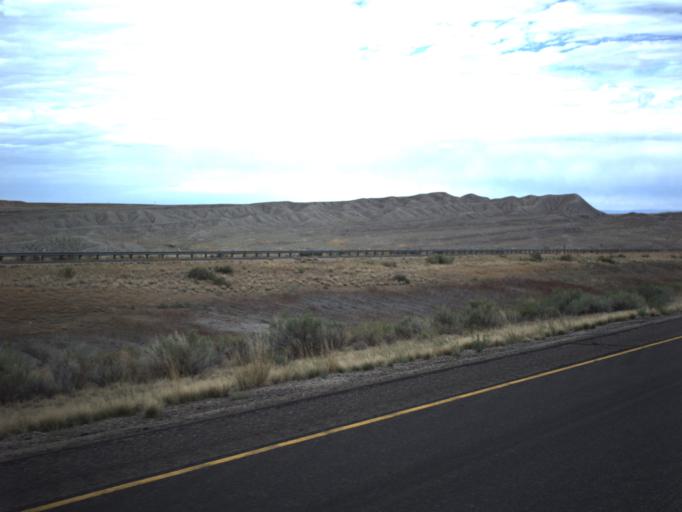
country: US
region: Utah
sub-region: Grand County
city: Moab
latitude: 38.9581
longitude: -109.7107
